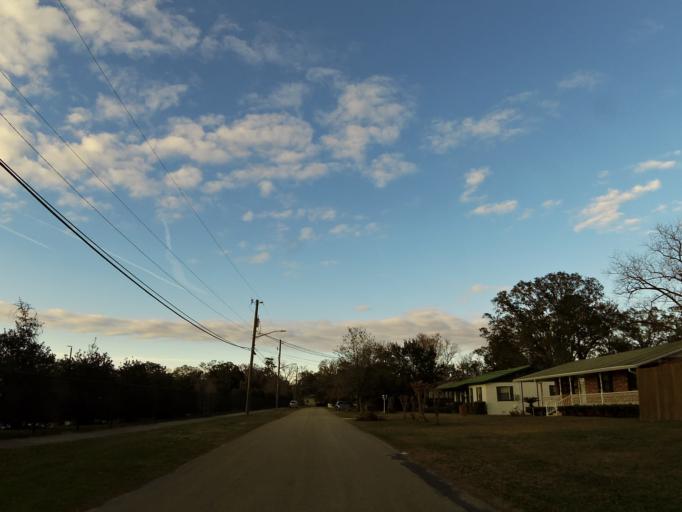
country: US
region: Florida
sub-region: Duval County
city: Jacksonville
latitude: 30.2976
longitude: -81.7284
